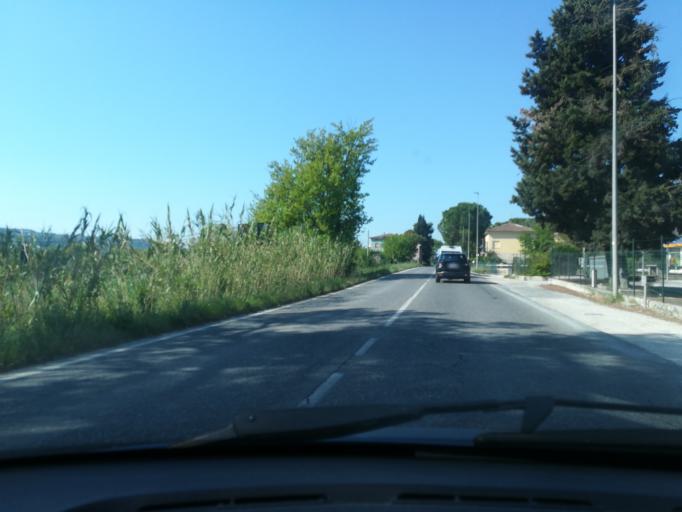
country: IT
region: The Marches
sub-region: Provincia di Macerata
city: Villa Potenza
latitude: 43.3277
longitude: 13.4220
